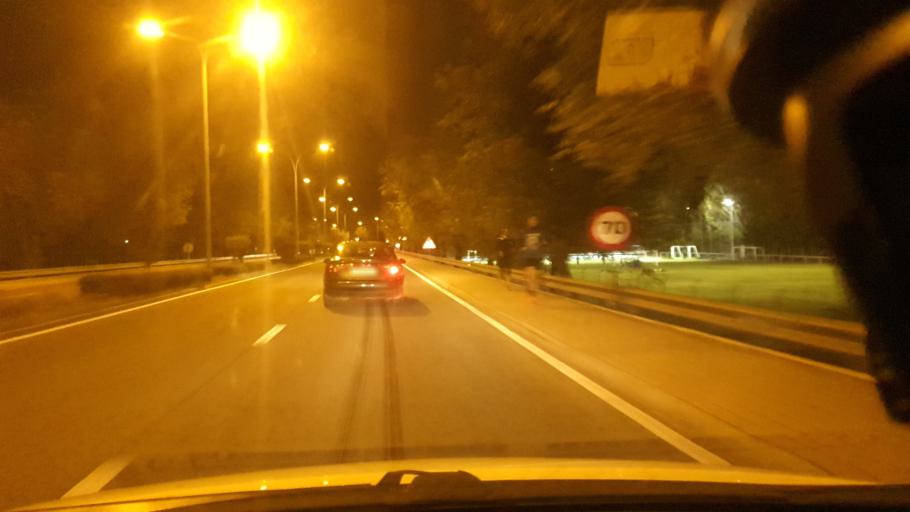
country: ES
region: Castille and Leon
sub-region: Provincia de Avila
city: Avila
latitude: 40.6496
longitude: -4.7063
